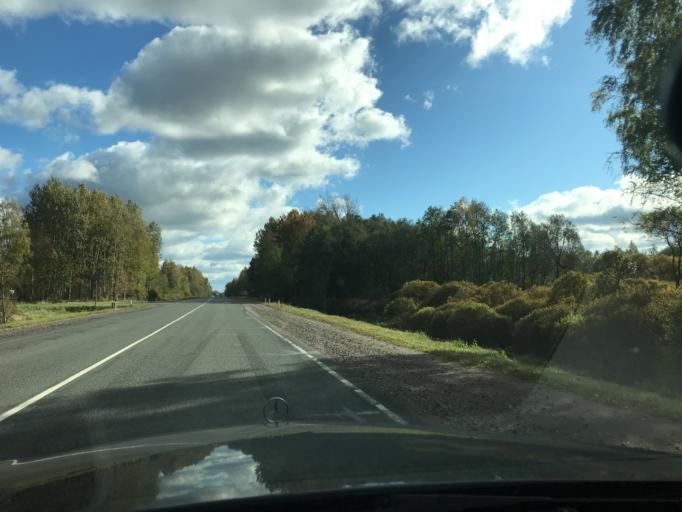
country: RU
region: Pskov
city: Ostrov
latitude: 57.2933
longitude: 28.3825
